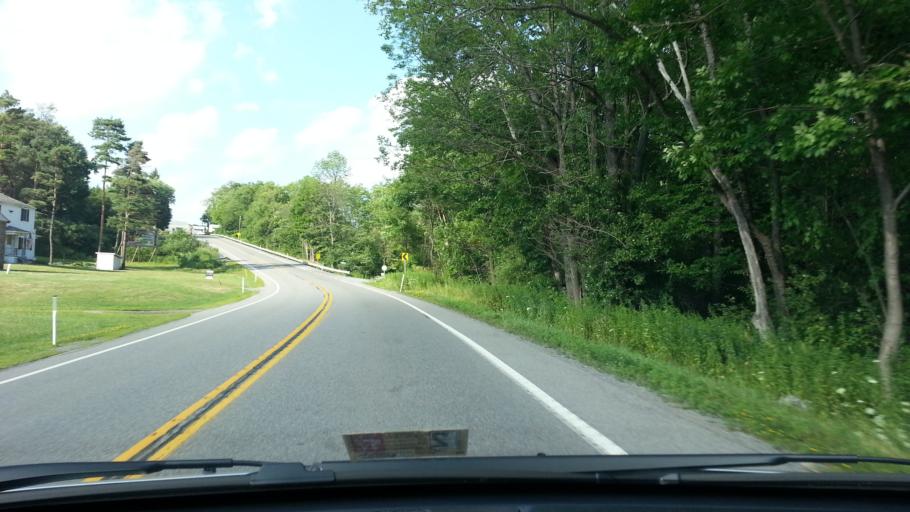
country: US
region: Pennsylvania
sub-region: Elk County
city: Saint Marys
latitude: 41.2544
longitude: -78.5035
